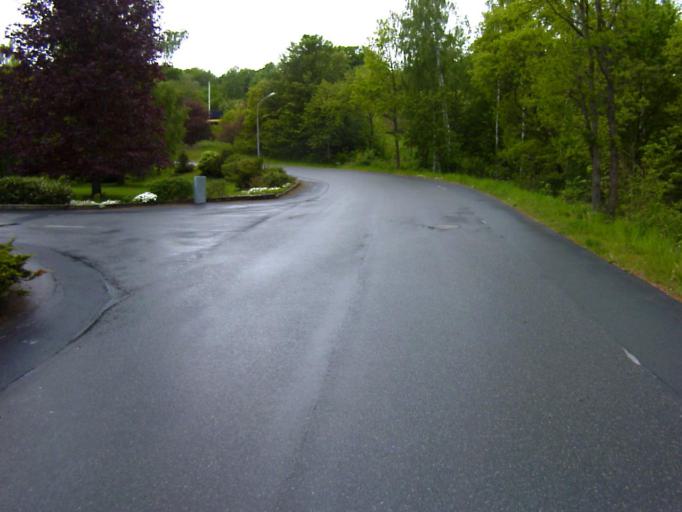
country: SE
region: Skane
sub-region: Kristianstads Kommun
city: Degeberga
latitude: 55.8293
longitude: 14.0817
